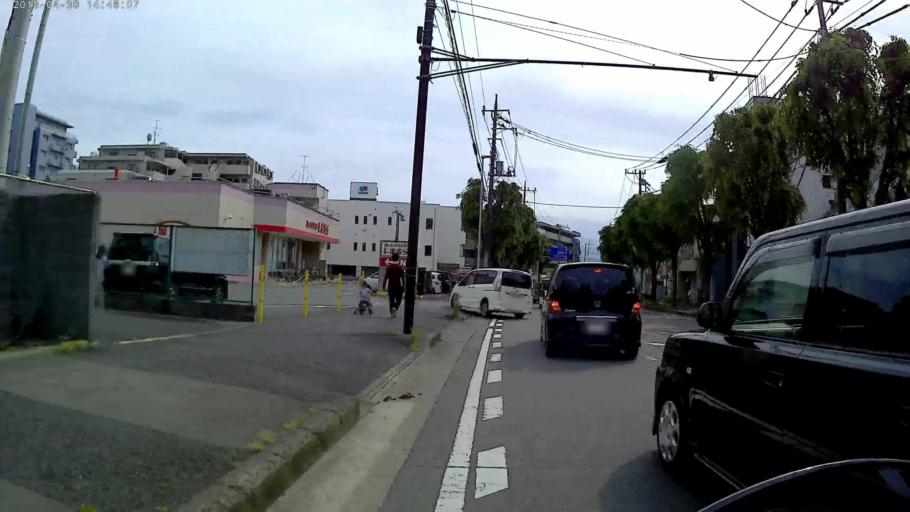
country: JP
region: Kanagawa
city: Zama
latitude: 35.5594
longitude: 139.3655
